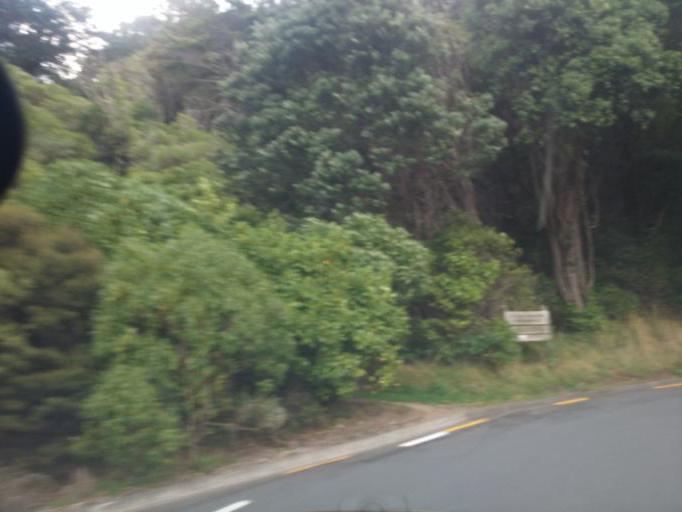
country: NZ
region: Wellington
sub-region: Wellington City
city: Kelburn
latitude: -41.2712
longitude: 174.7758
